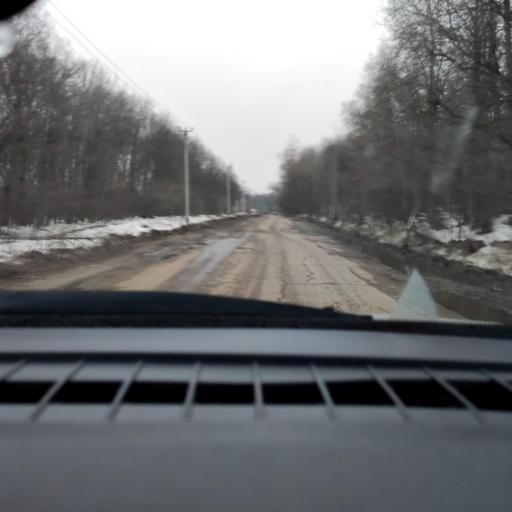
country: RU
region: Samara
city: Novosemeykino
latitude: 53.3338
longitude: 50.2715
